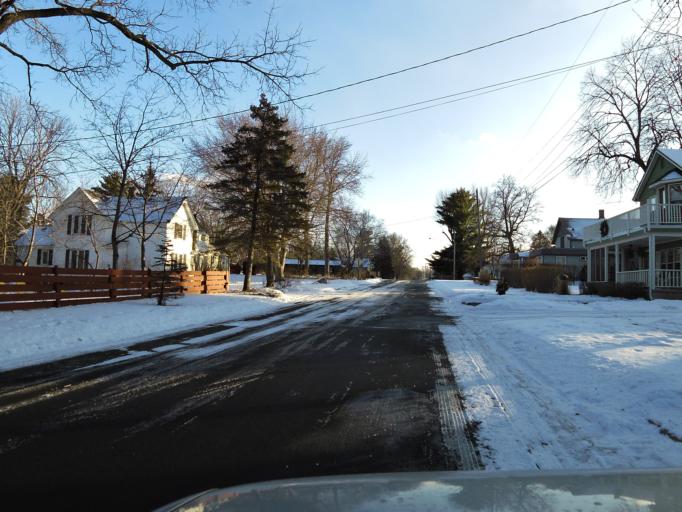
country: US
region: Minnesota
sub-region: Washington County
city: Stillwater
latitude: 45.0480
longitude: -92.8012
